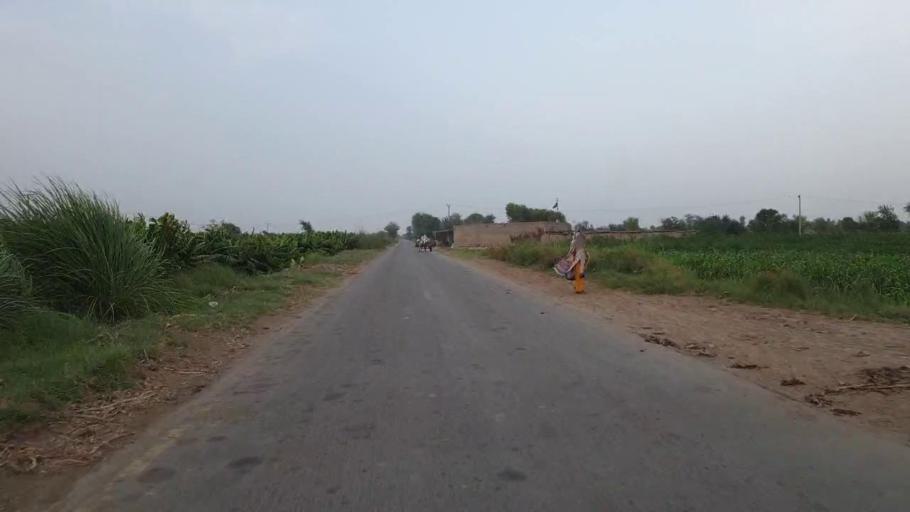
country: PK
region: Sindh
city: Daur
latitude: 26.4139
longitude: 68.2407
